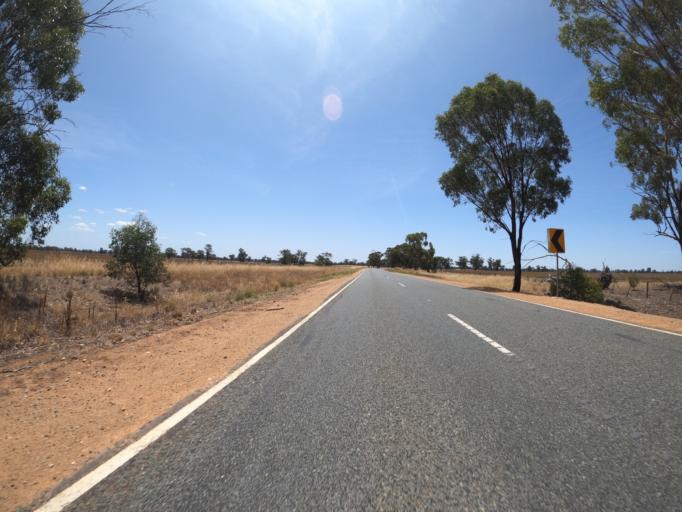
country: AU
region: Victoria
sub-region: Moira
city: Yarrawonga
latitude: -36.1978
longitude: 145.9671
